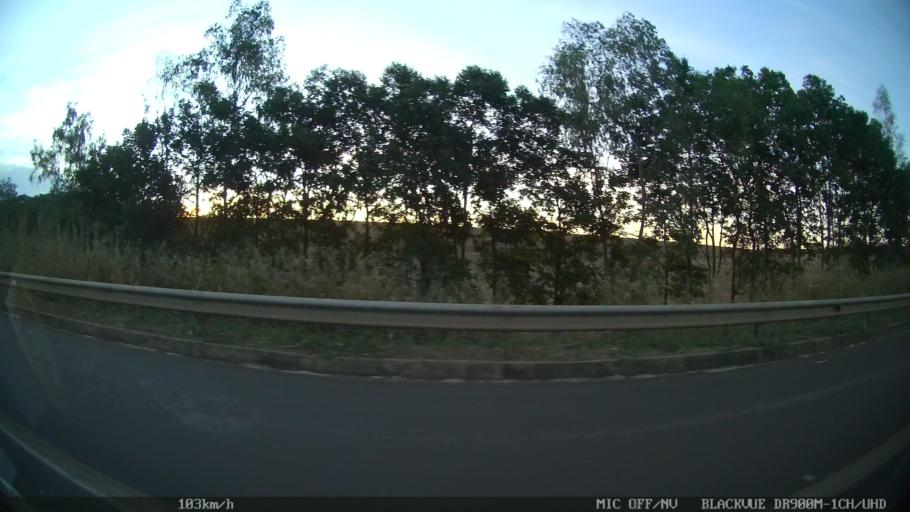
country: BR
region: Sao Paulo
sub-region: Catanduva
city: Catanduva
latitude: -21.1120
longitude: -48.9704
